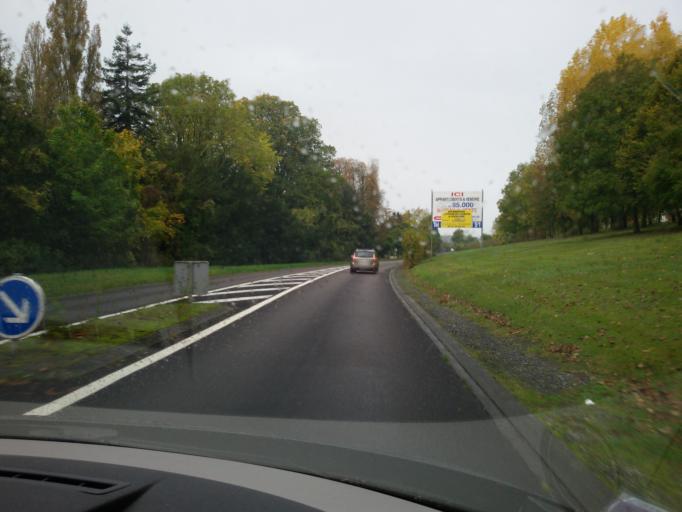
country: FR
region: Lower Normandy
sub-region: Departement du Calvados
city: Houlgate
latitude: 49.2977
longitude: -0.0617
